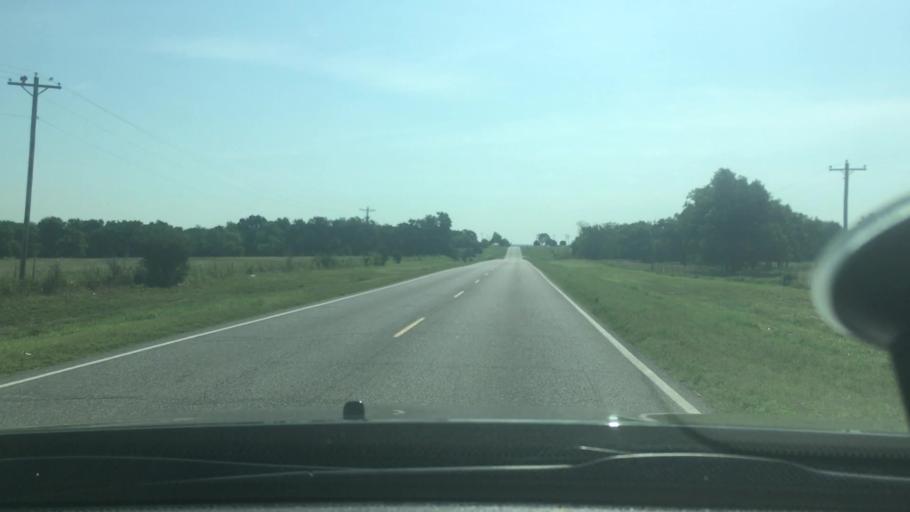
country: US
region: Oklahoma
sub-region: Garvin County
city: Wynnewood
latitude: 34.6517
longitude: -97.2344
